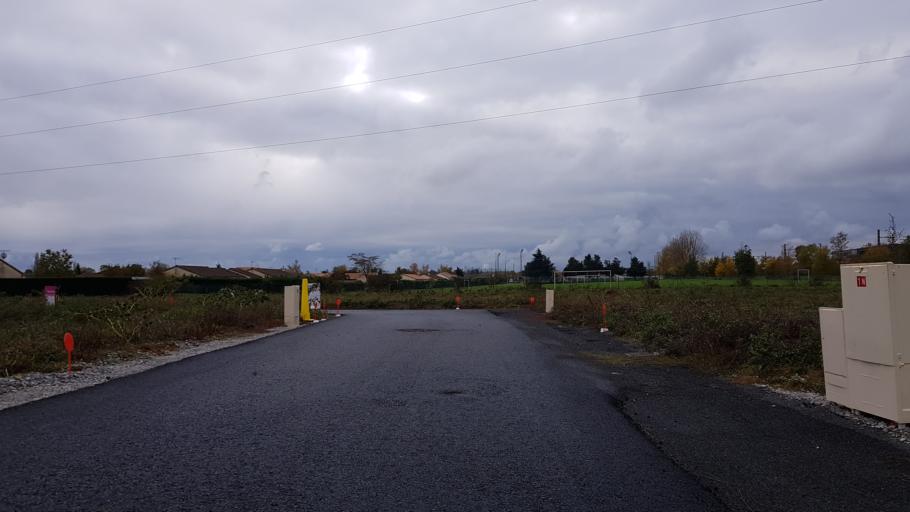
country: FR
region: Poitou-Charentes
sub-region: Departement de la Vienne
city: Chasseneuil-du-Poitou
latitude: 46.6615
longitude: 0.3791
